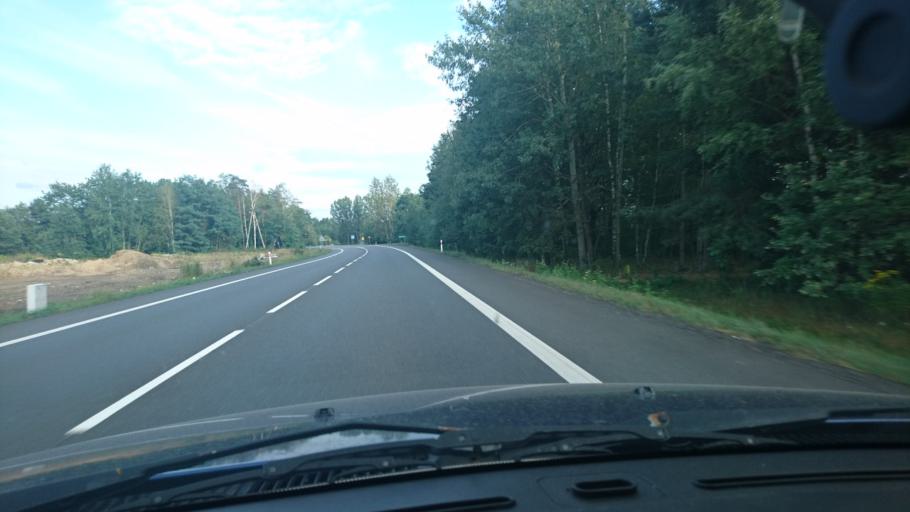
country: PL
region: Opole Voivodeship
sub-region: Powiat kluczborski
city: Kluczbork
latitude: 50.9687
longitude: 18.2672
